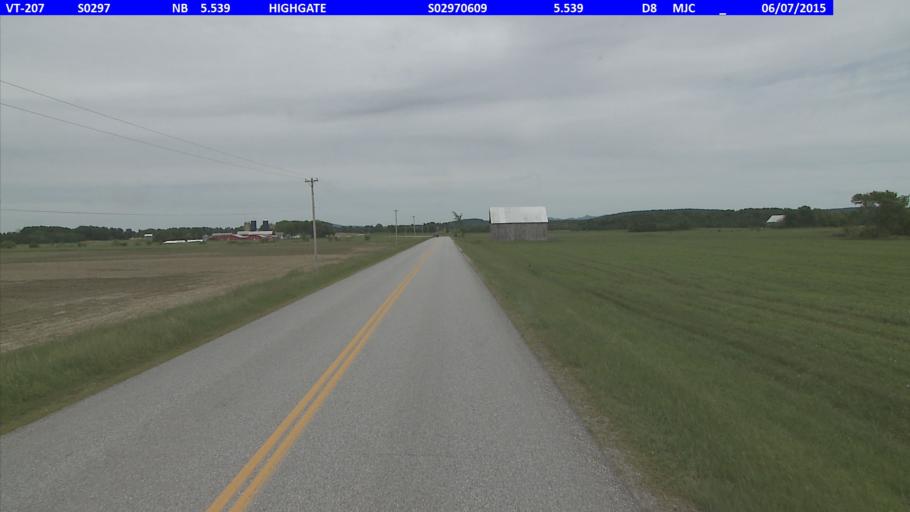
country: CA
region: Quebec
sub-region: Monteregie
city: Bedford
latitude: 45.0054
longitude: -72.9959
